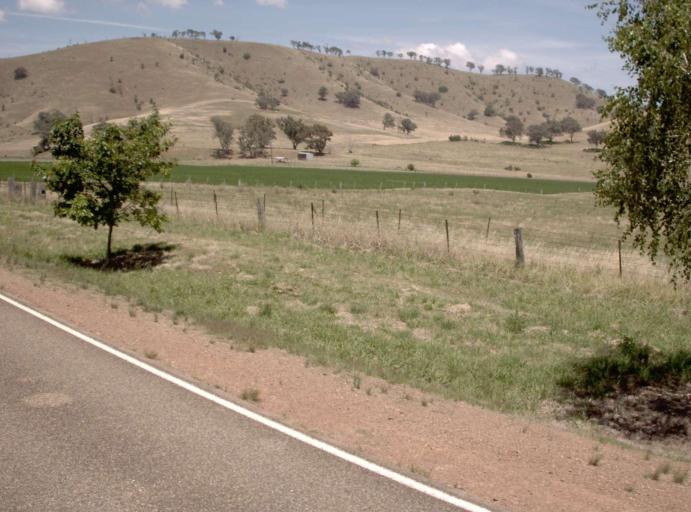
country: AU
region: Victoria
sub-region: East Gippsland
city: Bairnsdale
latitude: -37.2496
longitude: 147.7122
